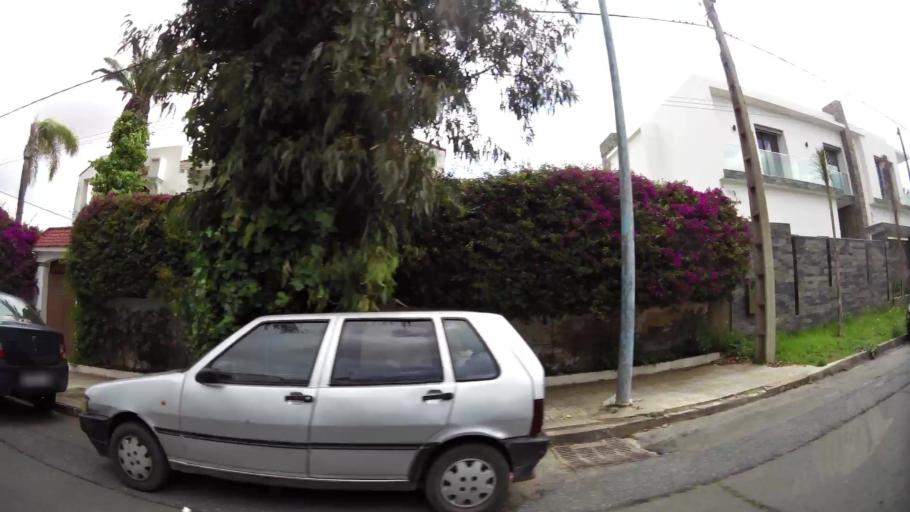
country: MA
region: Grand Casablanca
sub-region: Casablanca
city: Casablanca
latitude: 33.5611
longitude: -7.6190
